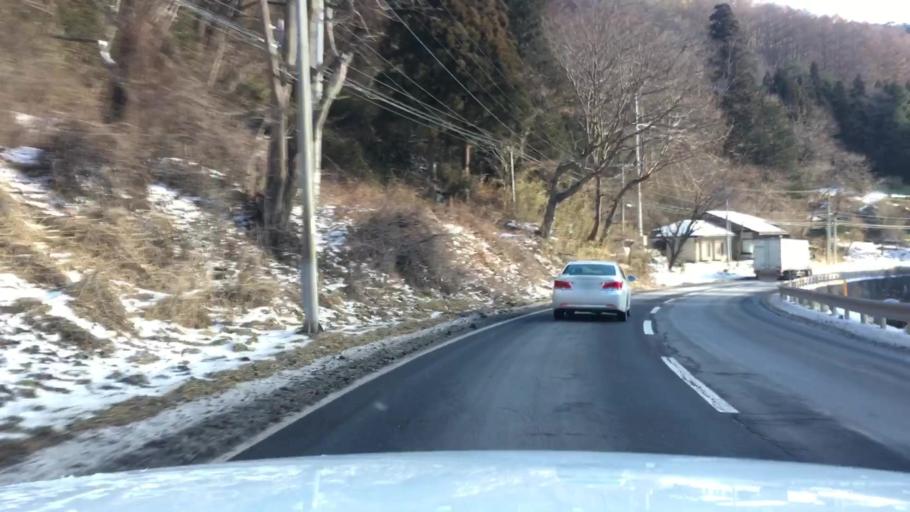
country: JP
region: Iwate
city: Tono
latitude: 39.6156
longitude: 141.4784
